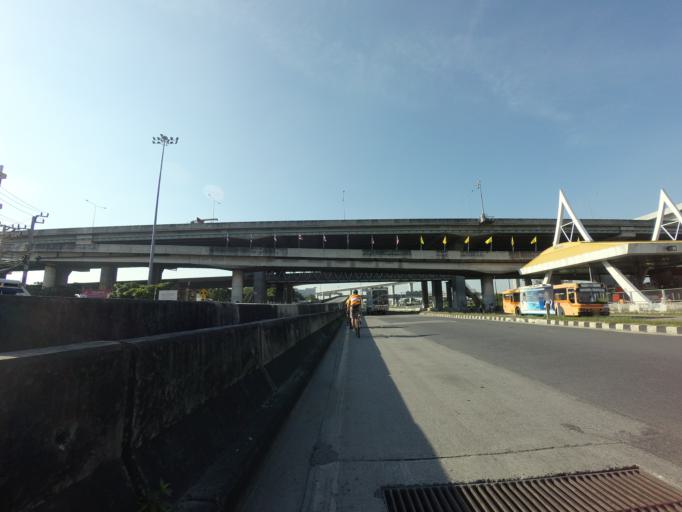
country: TH
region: Samut Prakan
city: Samut Prakan
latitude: 13.6306
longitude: 100.5892
